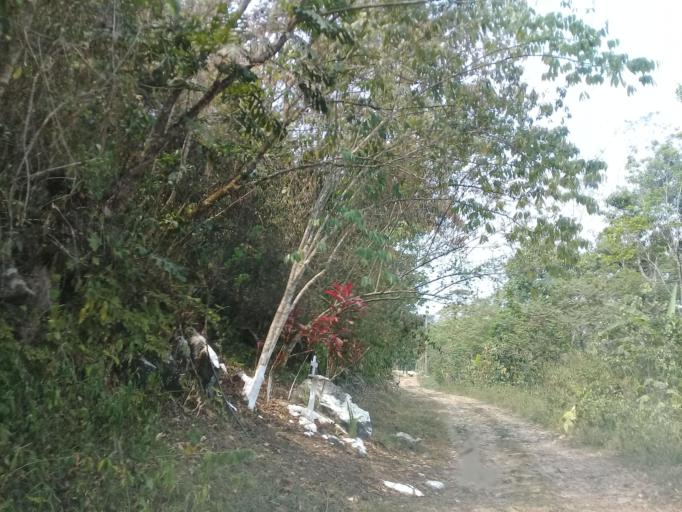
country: MX
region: Veracruz
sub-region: Tezonapa
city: Laguna Chica (Pueblo Nuevo)
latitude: 18.5852
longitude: -96.7474
